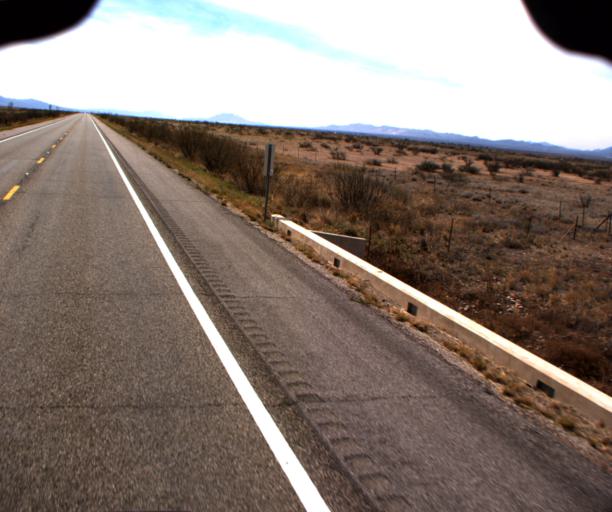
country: US
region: Arizona
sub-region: Cochise County
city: Pirtleville
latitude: 31.4928
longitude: -109.6311
